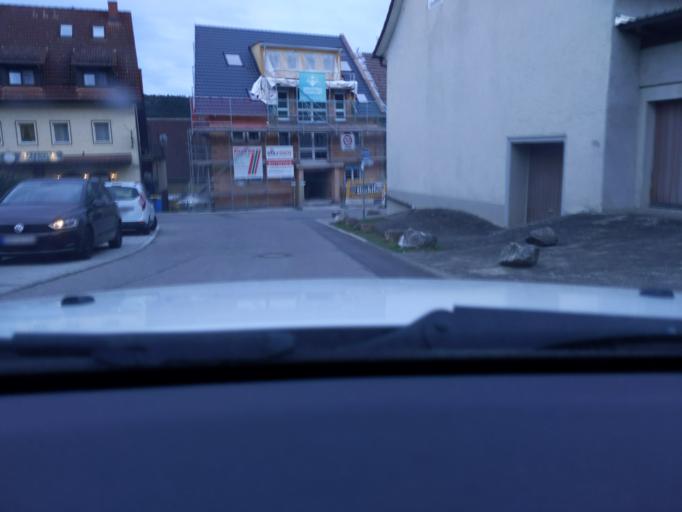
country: DE
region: Baden-Wuerttemberg
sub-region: Freiburg Region
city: Immendingen
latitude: 47.9581
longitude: 8.7617
